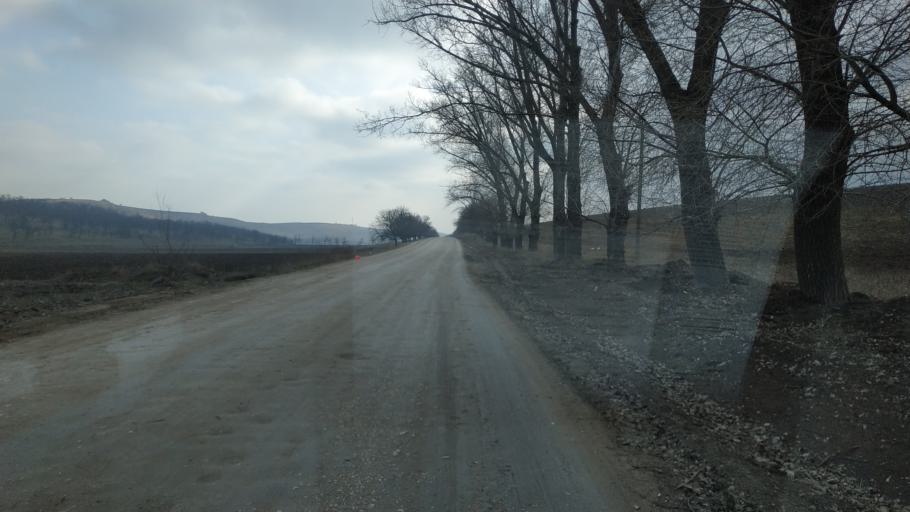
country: MD
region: Hincesti
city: Dancu
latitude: 46.9271
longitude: 28.3279
